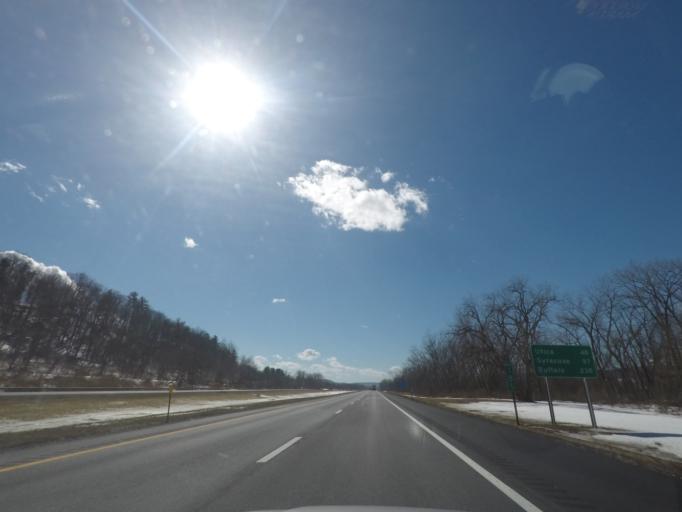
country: US
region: New York
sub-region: Montgomery County
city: Fonda
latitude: 42.9358
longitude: -74.4098
